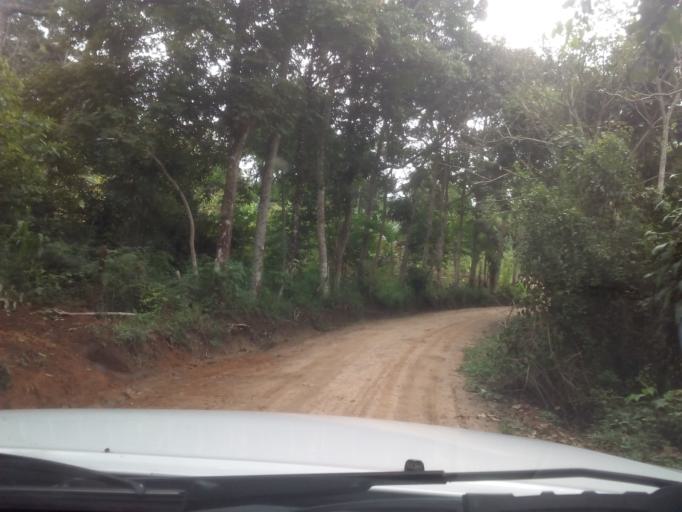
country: PE
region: San Martin
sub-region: Provincia de Lamas
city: Lamas
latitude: -6.4142
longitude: -76.4606
